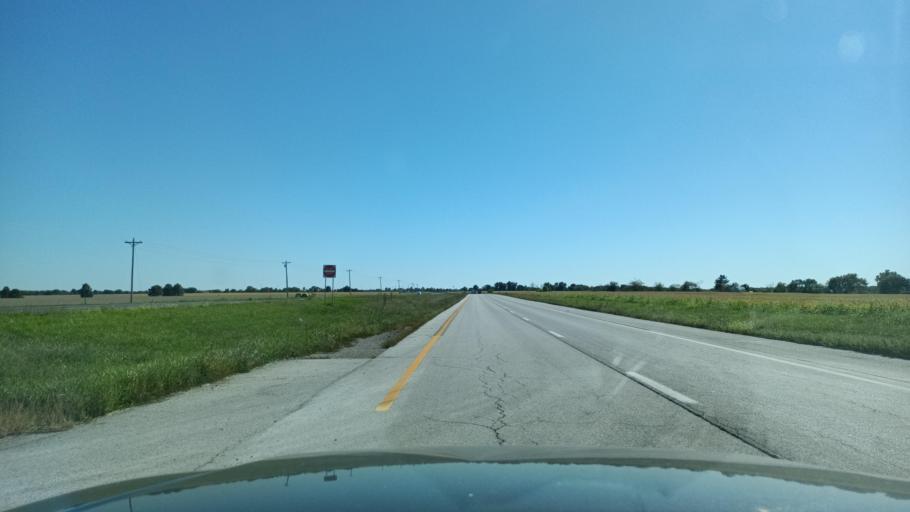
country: US
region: Missouri
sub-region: Macon County
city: Macon
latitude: 39.8172
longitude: -92.4729
